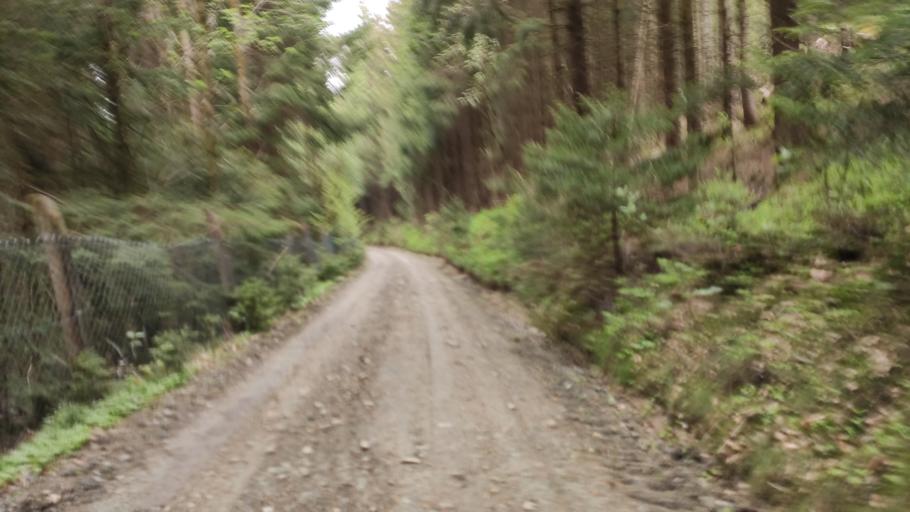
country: DE
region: Bavaria
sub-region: Upper Franconia
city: Tschirn
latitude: 50.4523
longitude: 11.4732
